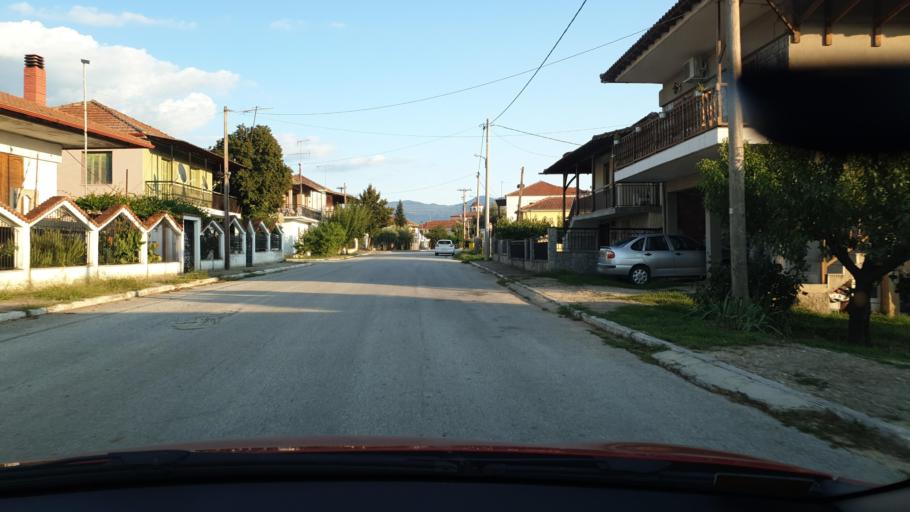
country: GR
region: Central Macedonia
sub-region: Nomos Thessalonikis
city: Nea Apollonia
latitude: 40.5479
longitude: 23.4475
